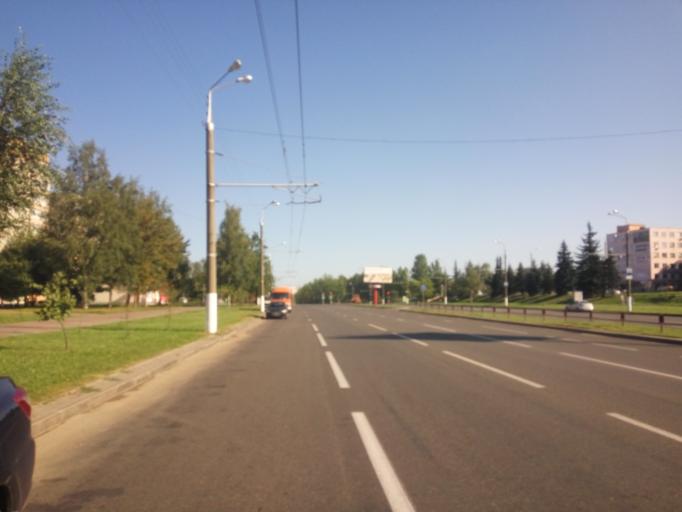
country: BY
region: Vitebsk
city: Vitebsk
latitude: 55.1913
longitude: 30.2497
